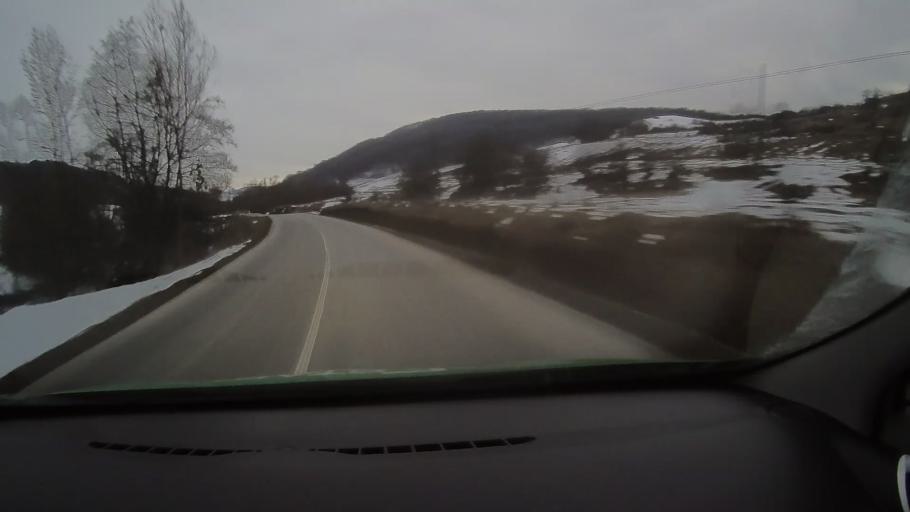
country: RO
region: Harghita
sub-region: Comuna Mugeni
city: Mugeni
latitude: 46.2292
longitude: 25.2388
